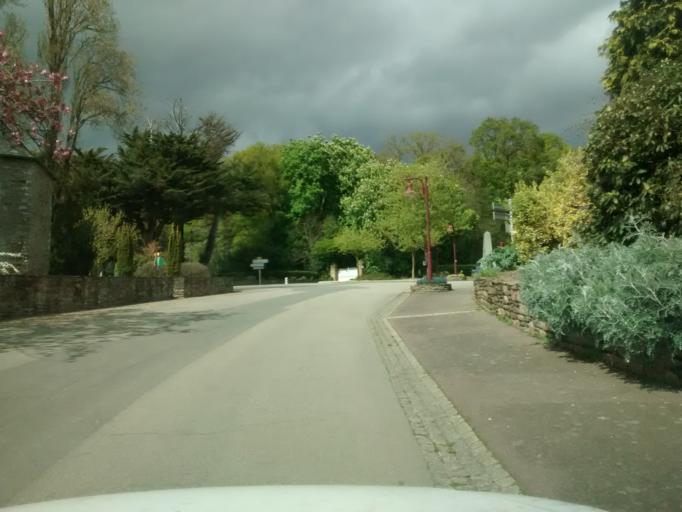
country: FR
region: Brittany
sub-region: Departement du Morbihan
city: Caro
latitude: 47.8363
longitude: -2.3505
